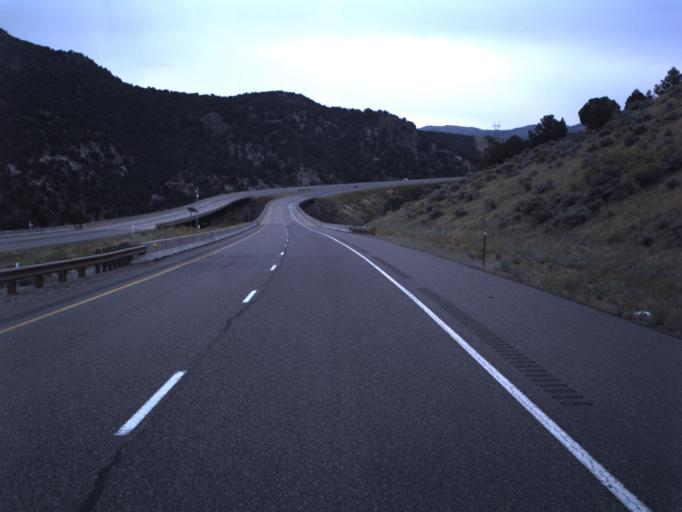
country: US
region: Utah
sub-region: Sevier County
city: Monroe
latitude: 38.5641
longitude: -112.4358
